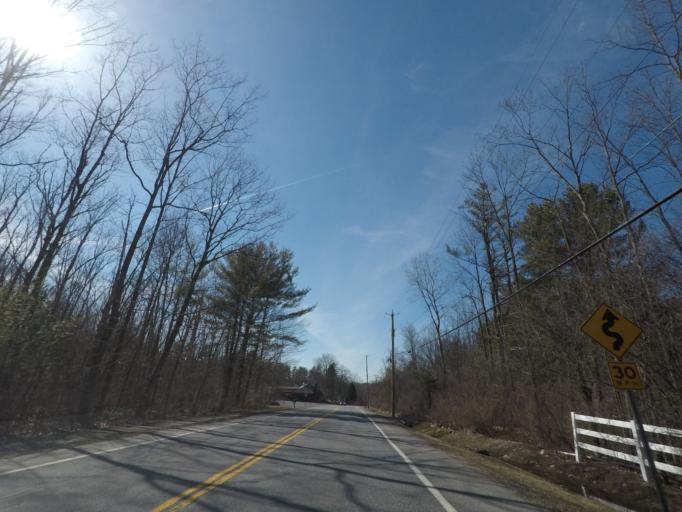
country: US
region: New York
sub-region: Saratoga County
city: Ballston Spa
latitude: 43.0007
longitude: -73.8285
